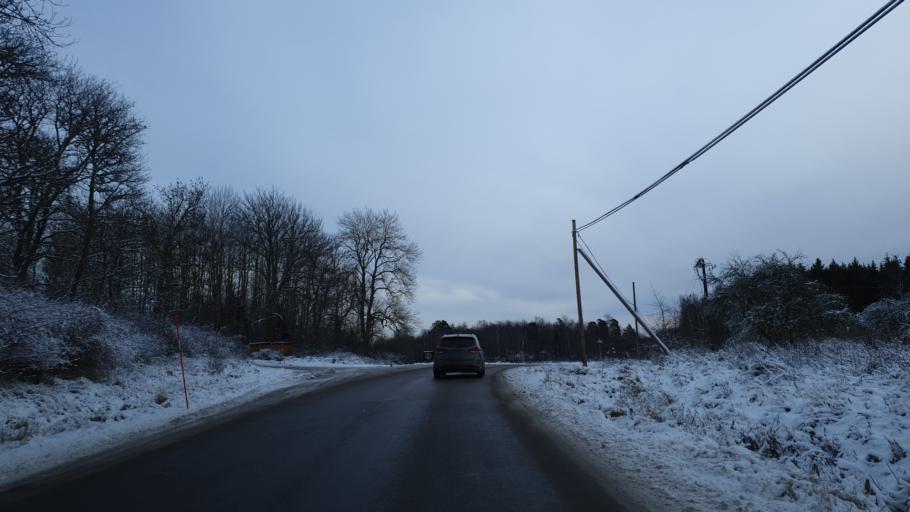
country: SE
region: Uppsala
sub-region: Uppsala Kommun
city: Saevja
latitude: 59.7070
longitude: 17.5978
